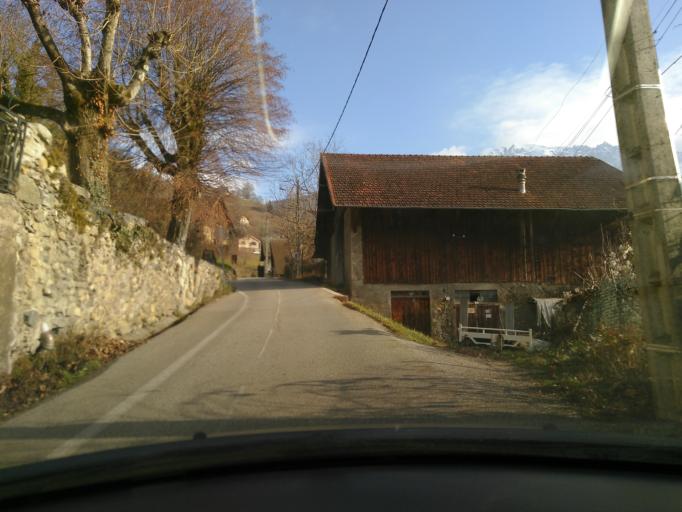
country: FR
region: Rhone-Alpes
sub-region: Departement de l'Isere
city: Villard-Bonnot
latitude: 45.2364
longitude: 5.9229
